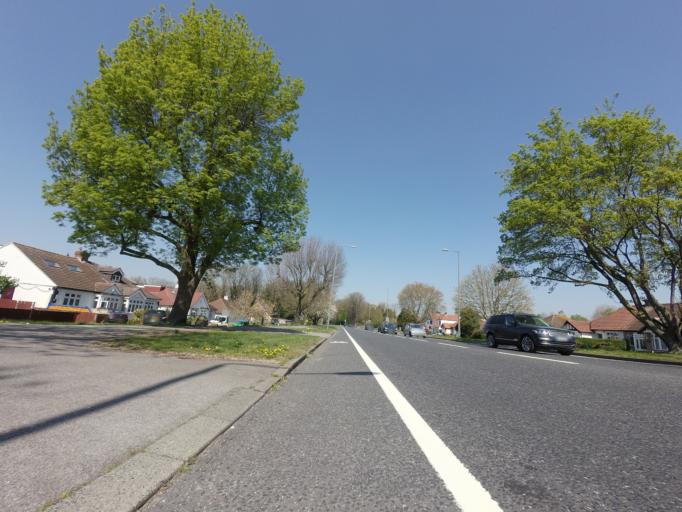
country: GB
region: England
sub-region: Greater London
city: Orpington
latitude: 51.3791
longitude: 0.1087
